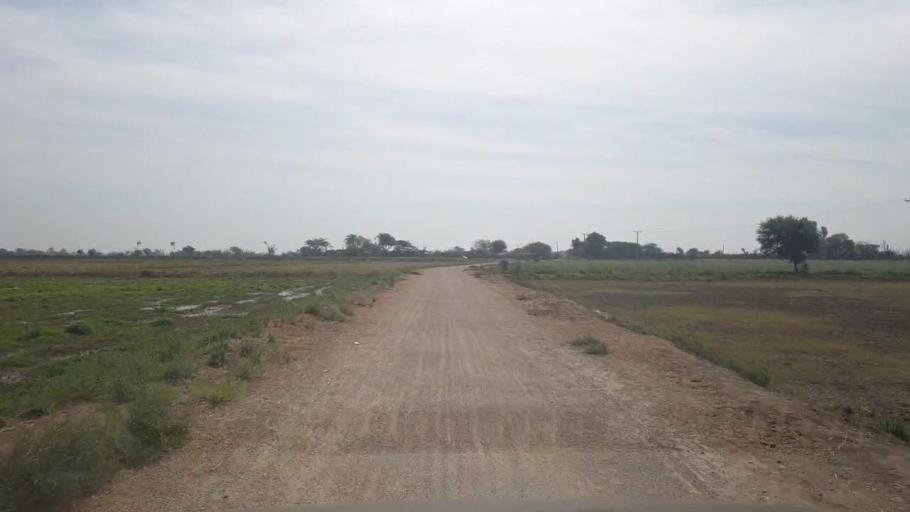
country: PK
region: Sindh
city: Umarkot
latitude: 25.3557
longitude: 69.6061
